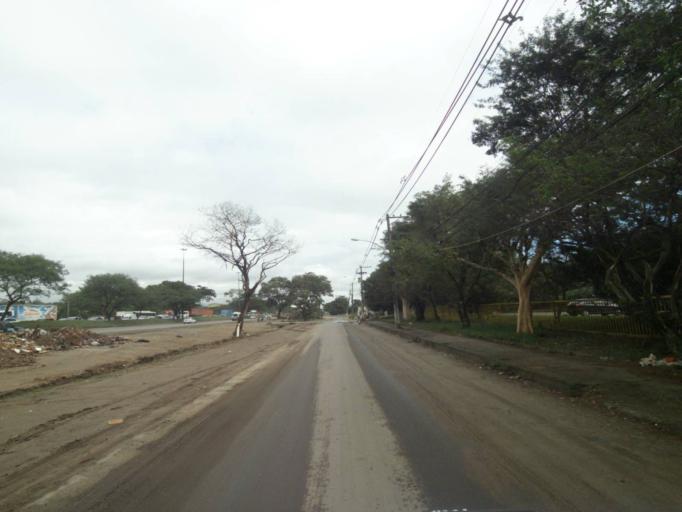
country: BR
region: Rio de Janeiro
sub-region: Nilopolis
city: Nilopolis
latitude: -22.8571
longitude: -43.4984
